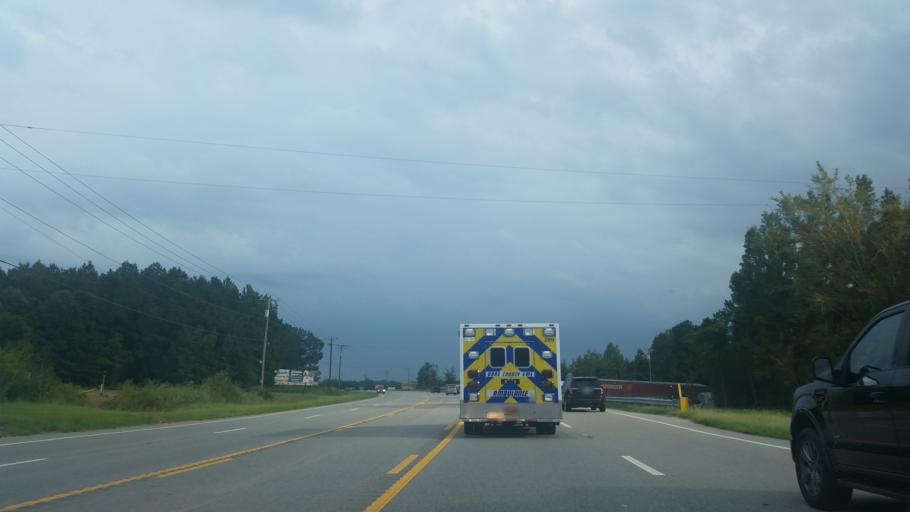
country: US
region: North Carolina
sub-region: Currituck County
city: Moyock
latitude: 36.4806
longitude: -76.1312
